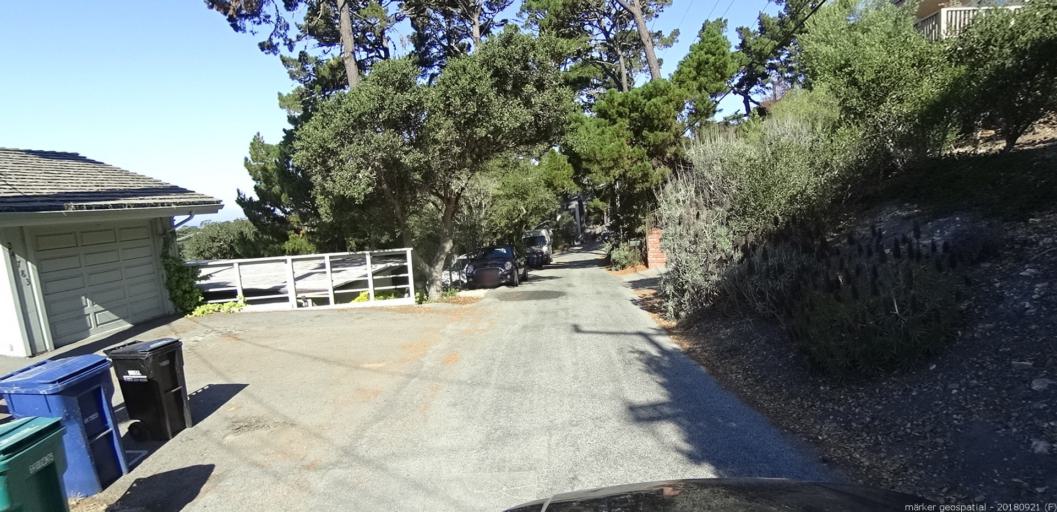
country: US
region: California
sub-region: Monterey County
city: Carmel-by-the-Sea
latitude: 36.5628
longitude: -121.9144
